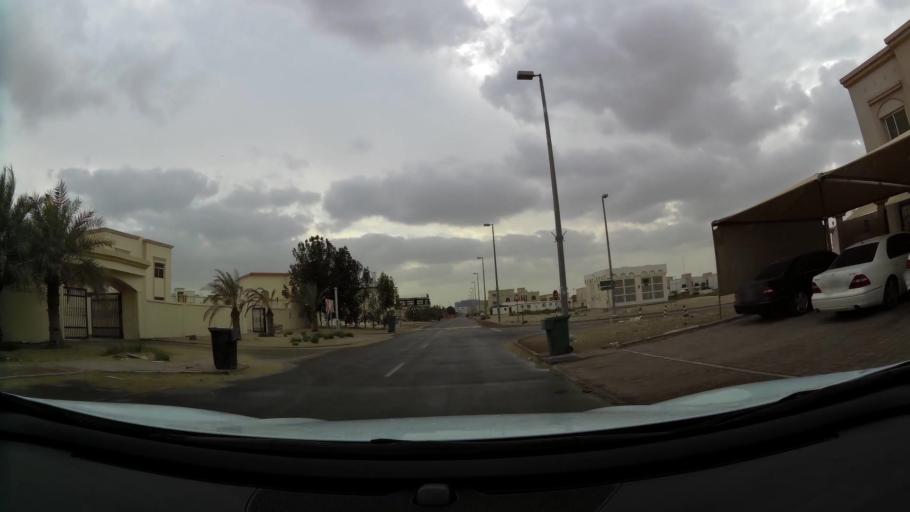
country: AE
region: Abu Dhabi
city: Abu Dhabi
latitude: 24.3482
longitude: 54.6337
